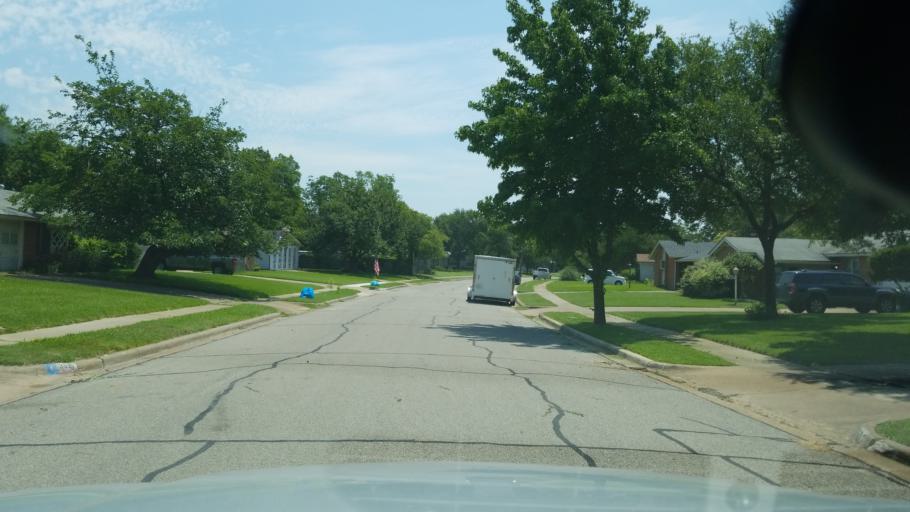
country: US
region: Texas
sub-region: Dallas County
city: Irving
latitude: 32.8503
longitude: -96.9495
